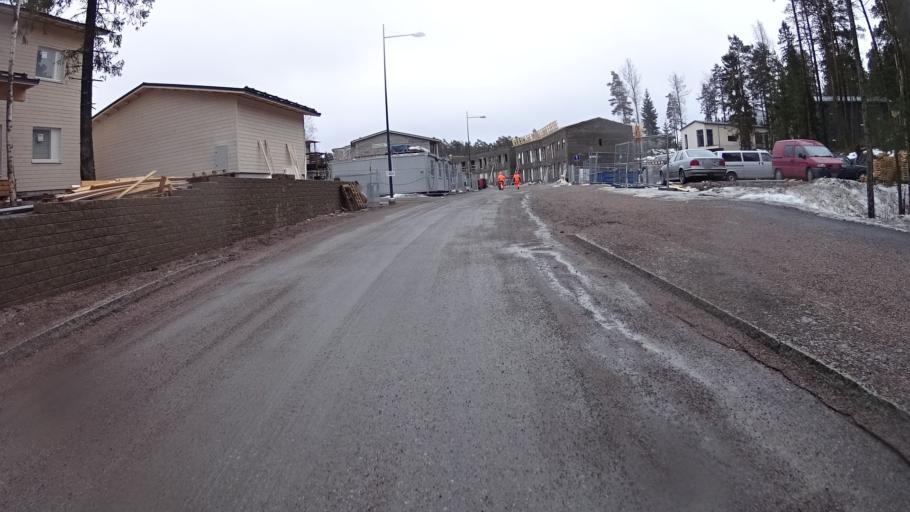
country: FI
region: Uusimaa
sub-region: Helsinki
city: Espoo
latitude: 60.2002
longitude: 24.6061
